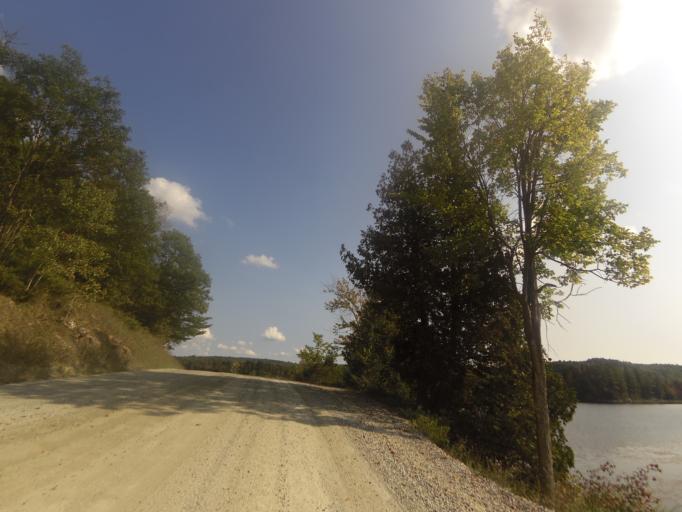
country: CA
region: Ontario
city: Renfrew
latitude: 45.1345
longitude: -76.6430
